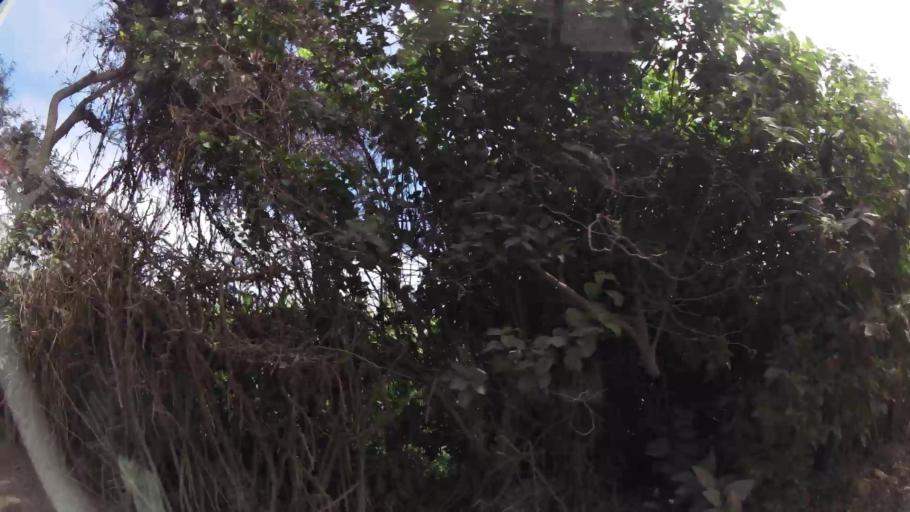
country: PE
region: Lima
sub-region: Provincia de Canete
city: Mala
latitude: -12.7328
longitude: -76.6229
